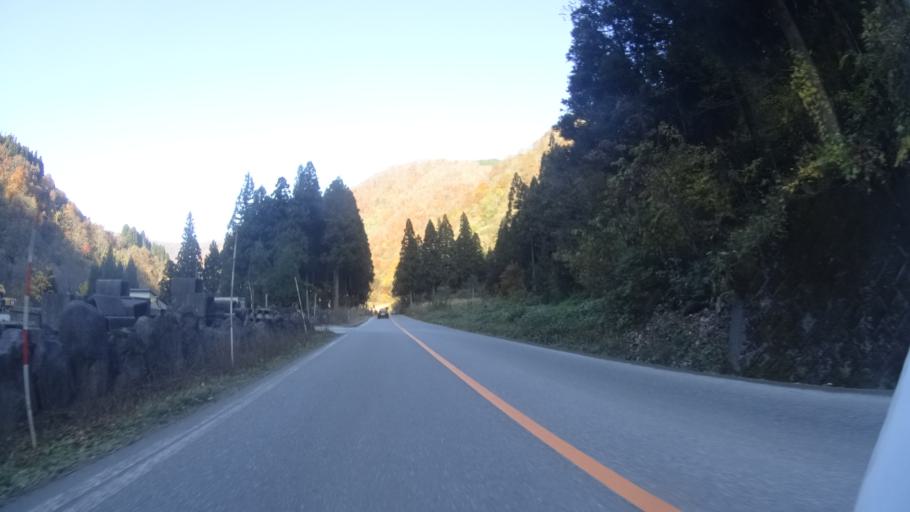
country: JP
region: Fukui
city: Ono
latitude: 35.9288
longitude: 136.6334
